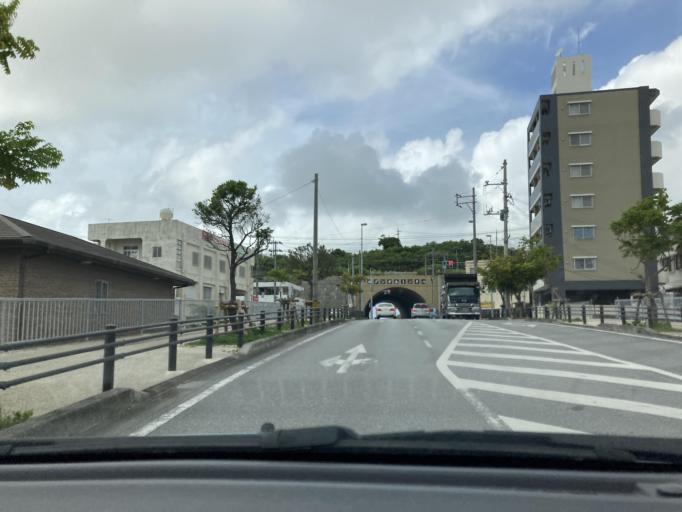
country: JP
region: Okinawa
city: Ginowan
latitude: 26.2361
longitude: 127.7340
